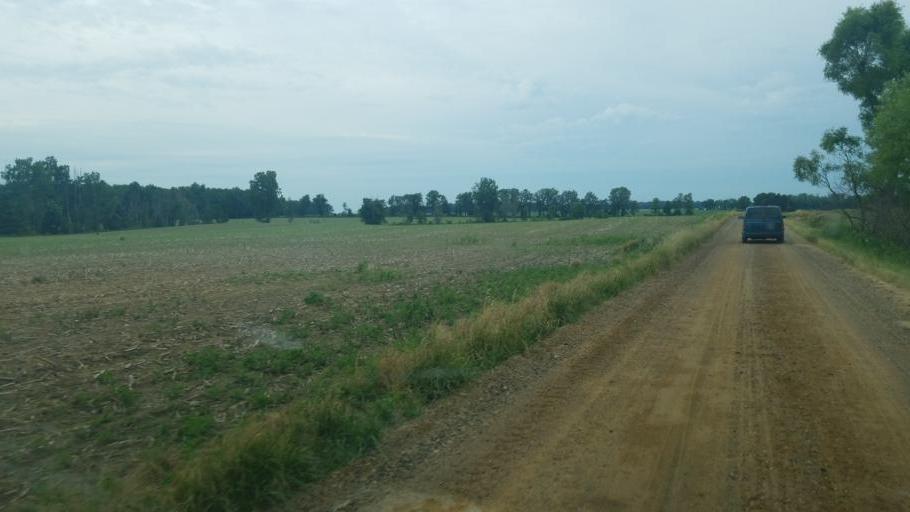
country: US
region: Michigan
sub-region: Barry County
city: Nashville
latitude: 42.6571
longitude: -84.9754
